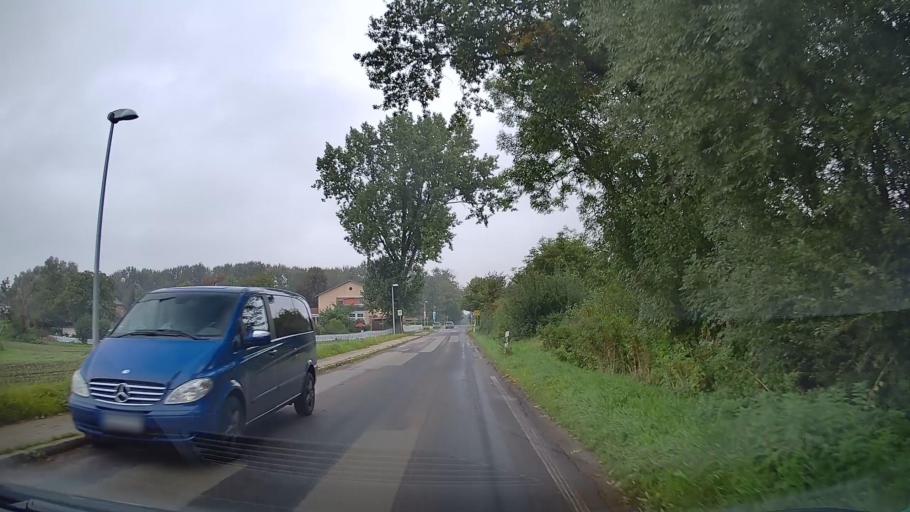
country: DE
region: Mecklenburg-Vorpommern
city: Hornstorf
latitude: 53.9158
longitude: 11.5329
